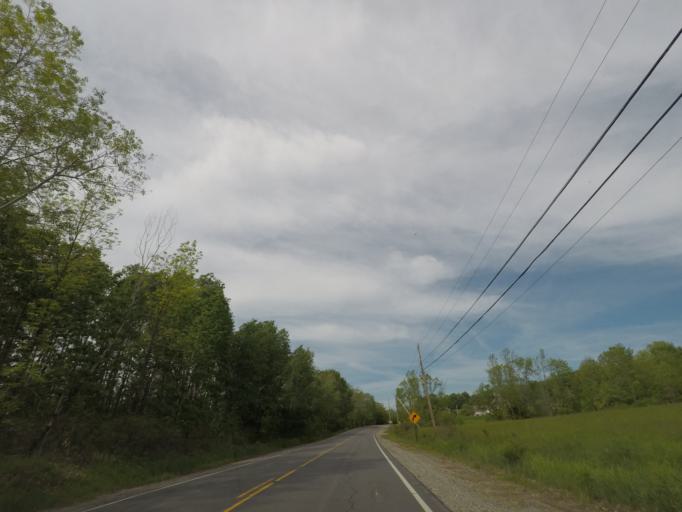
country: US
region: Maine
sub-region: Sagadahoc County
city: Richmond
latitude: 44.1006
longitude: -69.7302
